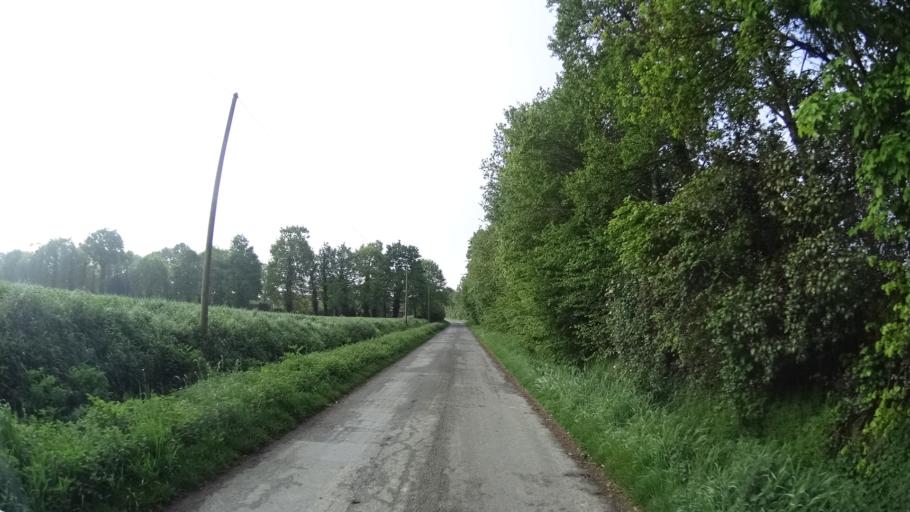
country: FR
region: Brittany
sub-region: Departement d'Ille-et-Vilaine
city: Mordelles
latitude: 48.0890
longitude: -1.8558
